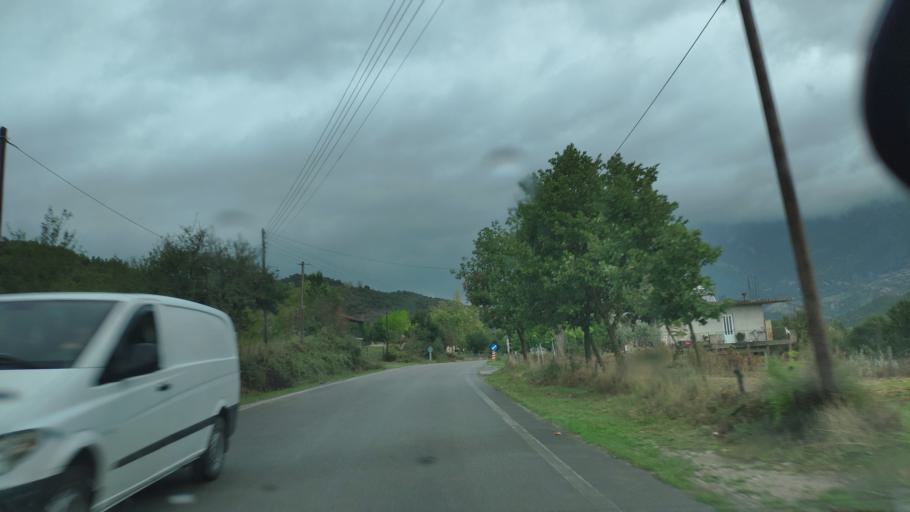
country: GR
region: West Greece
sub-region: Nomos Aitolias kai Akarnanias
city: Krikellos
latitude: 39.0027
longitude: 21.3093
